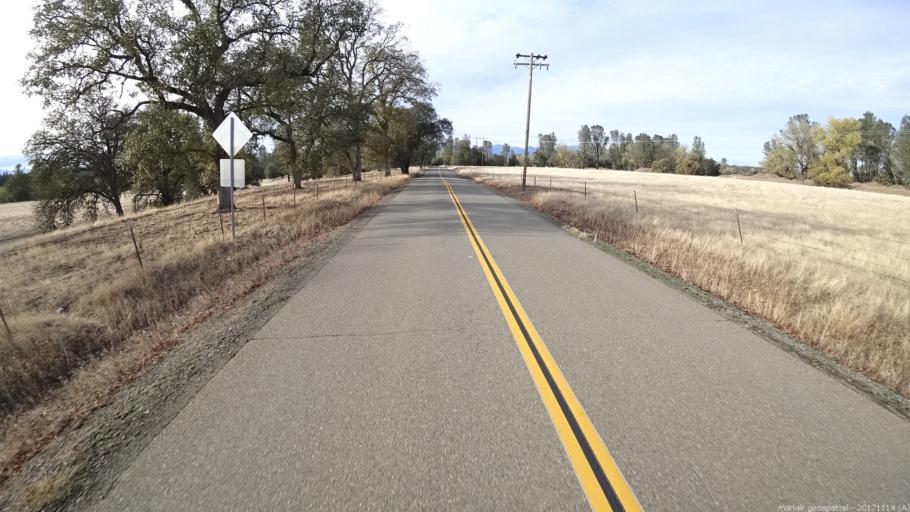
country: US
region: California
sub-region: Shasta County
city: Shasta
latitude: 40.3923
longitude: -122.5078
